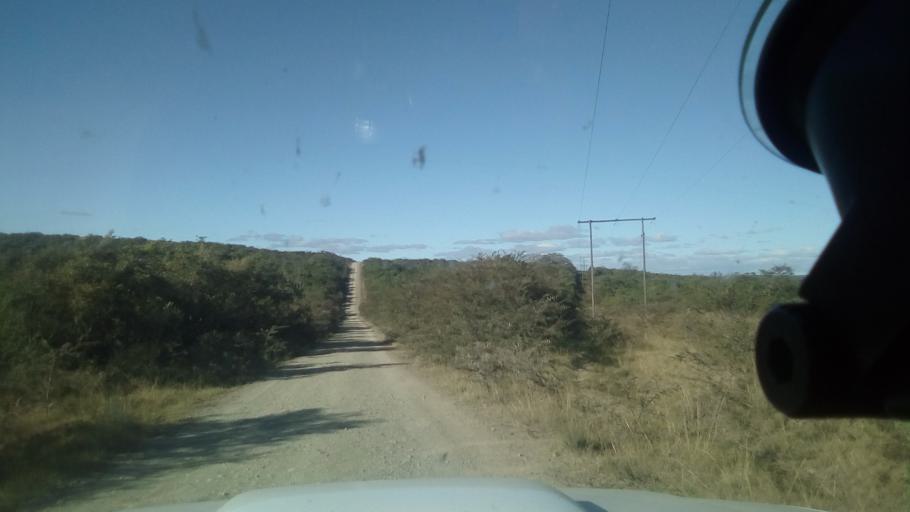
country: ZA
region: Eastern Cape
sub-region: Buffalo City Metropolitan Municipality
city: Bhisho
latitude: -32.7530
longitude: 27.3402
